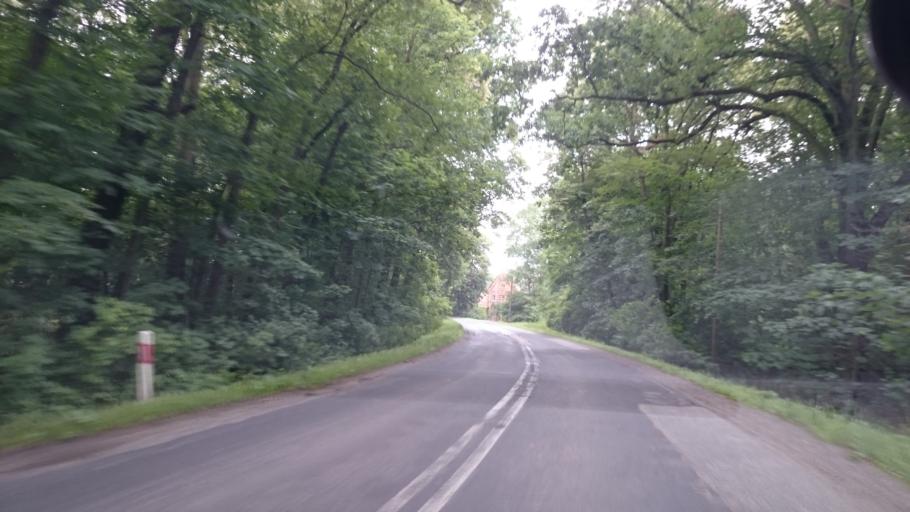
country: PL
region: Opole Voivodeship
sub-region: Powiat brzeski
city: Grodkow
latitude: 50.6487
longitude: 17.4409
